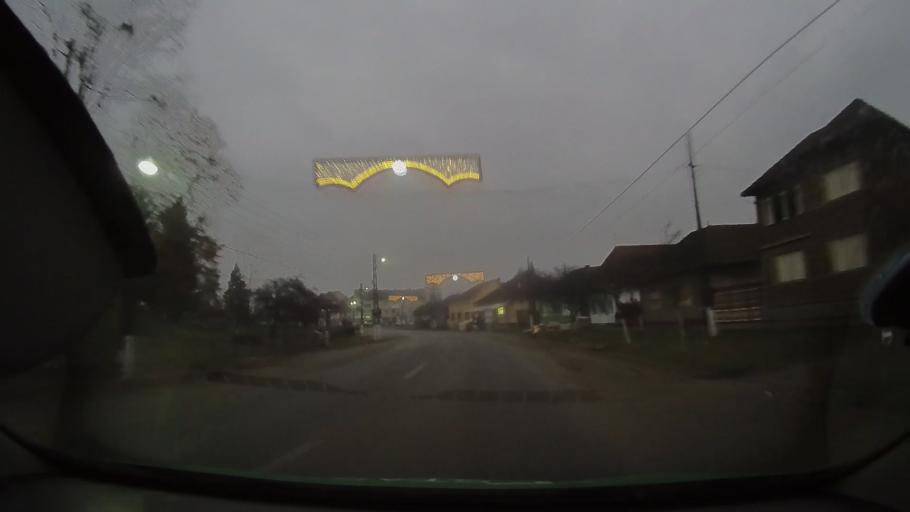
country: RO
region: Arad
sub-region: Comuna Beliu
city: Beliu
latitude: 46.4937
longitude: 21.9829
